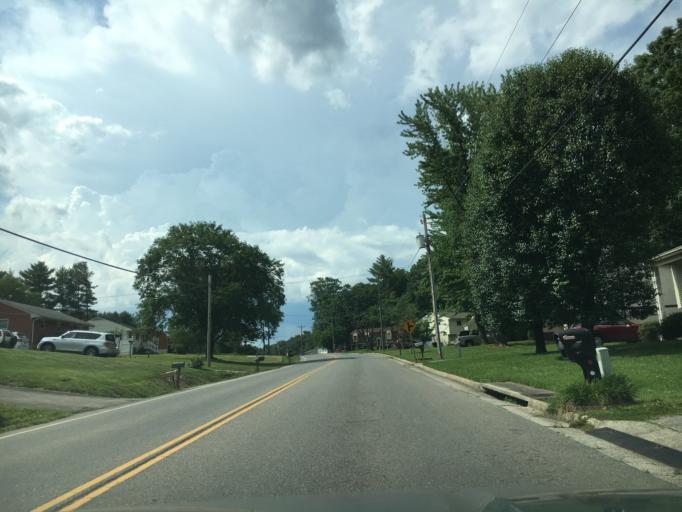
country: US
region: Virginia
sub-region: Roanoke County
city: Cave Spring
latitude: 37.2070
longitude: -80.0091
